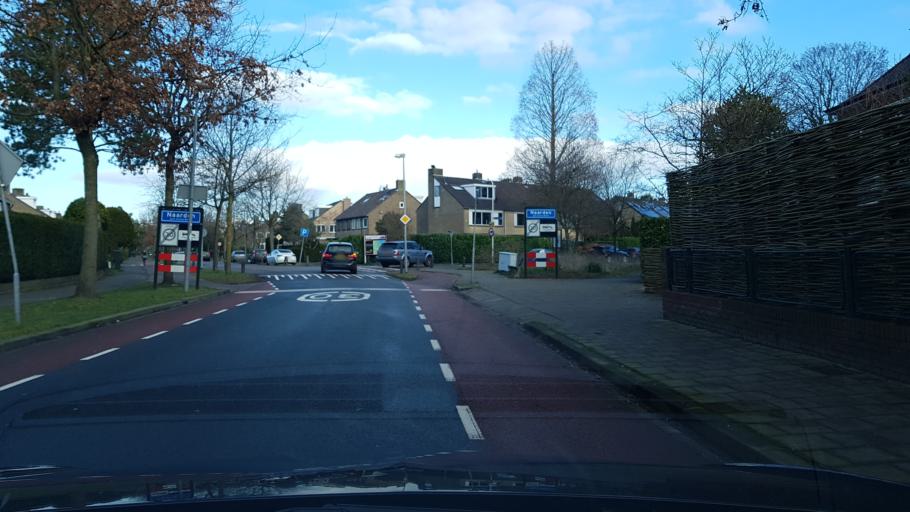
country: NL
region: North Holland
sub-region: Gemeente Bussum
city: Bussum
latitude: 52.2788
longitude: 5.1475
